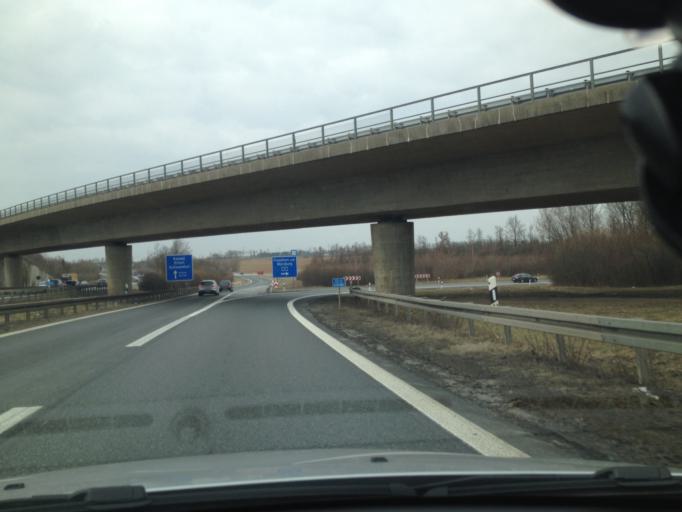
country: DE
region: Bavaria
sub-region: Regierungsbezirk Unterfranken
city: Biebelried
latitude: 49.7798
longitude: 10.0913
